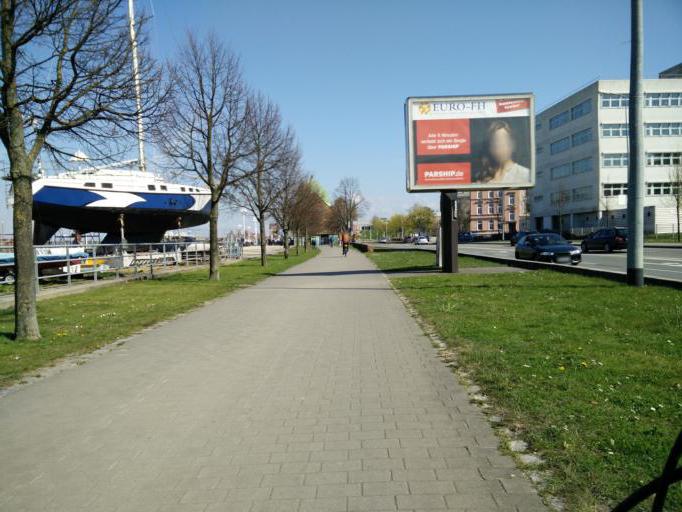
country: DE
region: Mecklenburg-Vorpommern
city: Rostock
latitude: 54.0922
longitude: 12.1237
